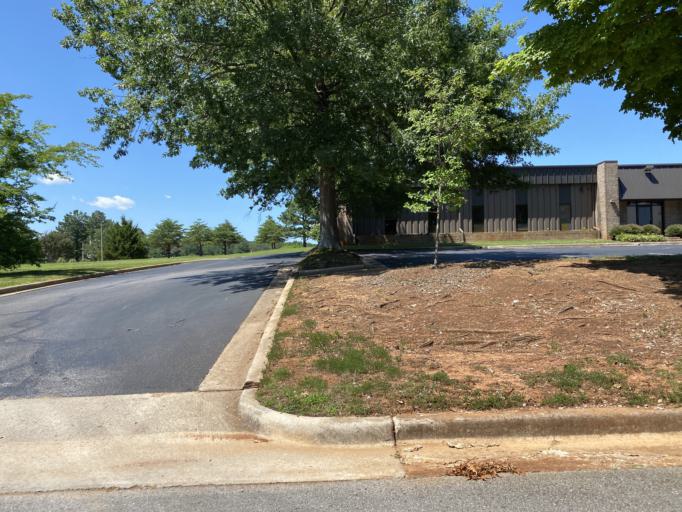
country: US
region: Alabama
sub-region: Madison County
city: Redstone Arsenal
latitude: 34.7433
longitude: -86.6581
